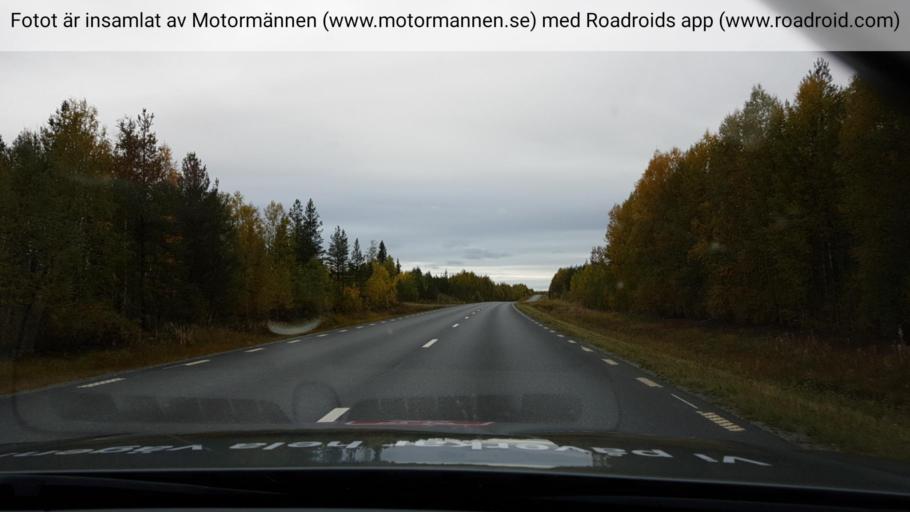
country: SE
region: Vaesterbotten
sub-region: Dorotea Kommun
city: Dorotea
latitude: 64.3295
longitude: 16.6291
